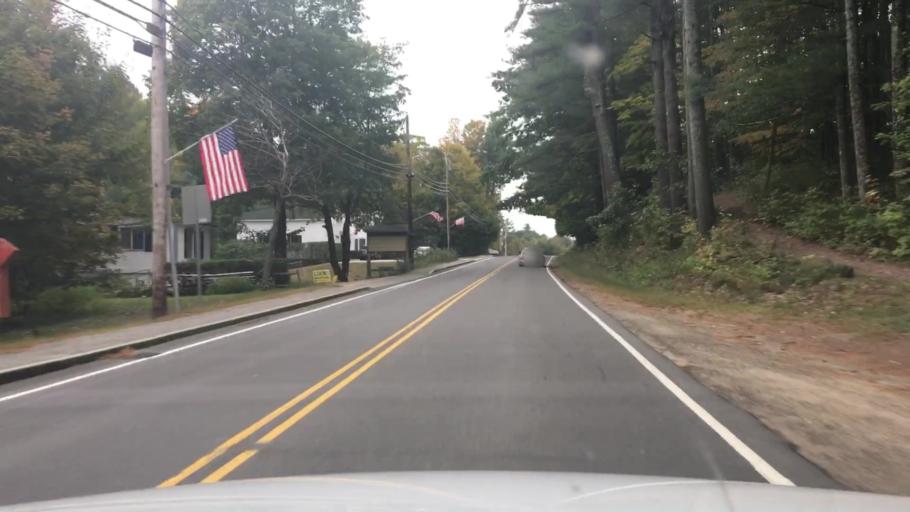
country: US
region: New Hampshire
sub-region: Strafford County
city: New Durham
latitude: 43.4673
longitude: -71.2311
